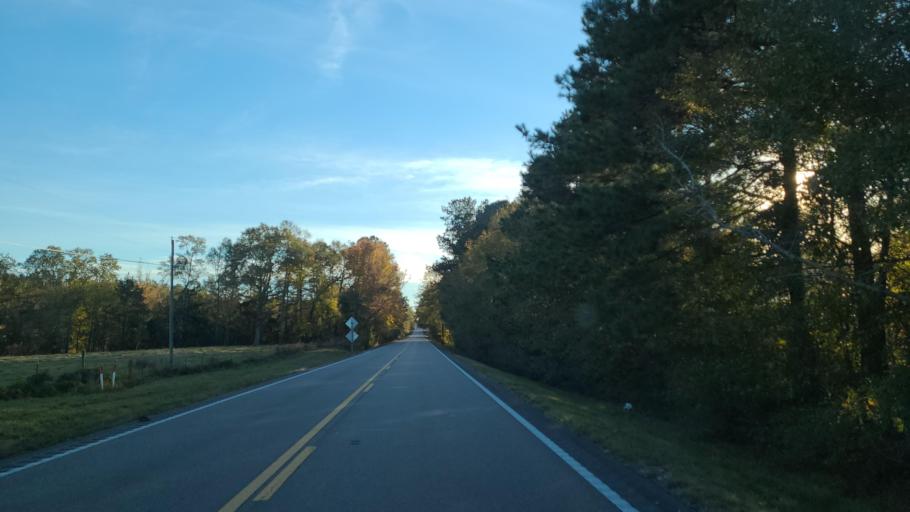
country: US
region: Mississippi
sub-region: Lamar County
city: Lumberton
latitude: 31.0373
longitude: -89.4403
